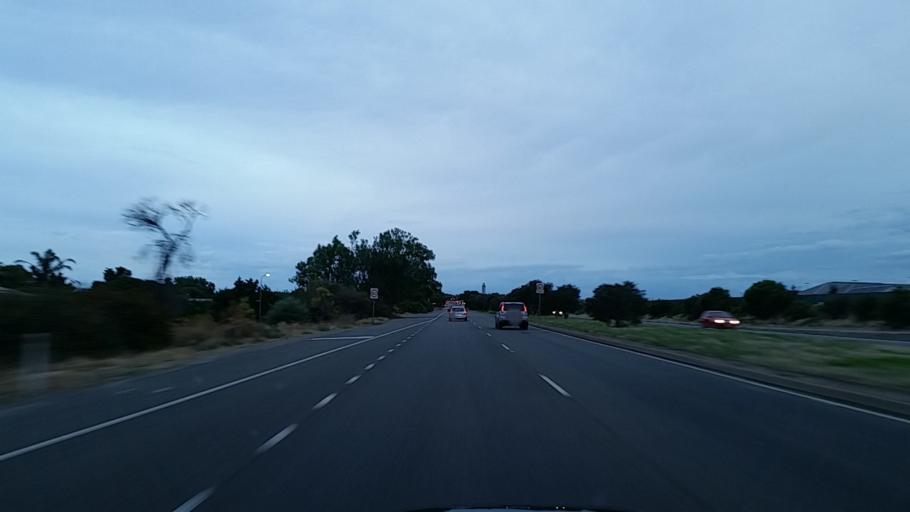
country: AU
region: South Australia
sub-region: Marion
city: Happy Valley
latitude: -35.0829
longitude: 138.5114
